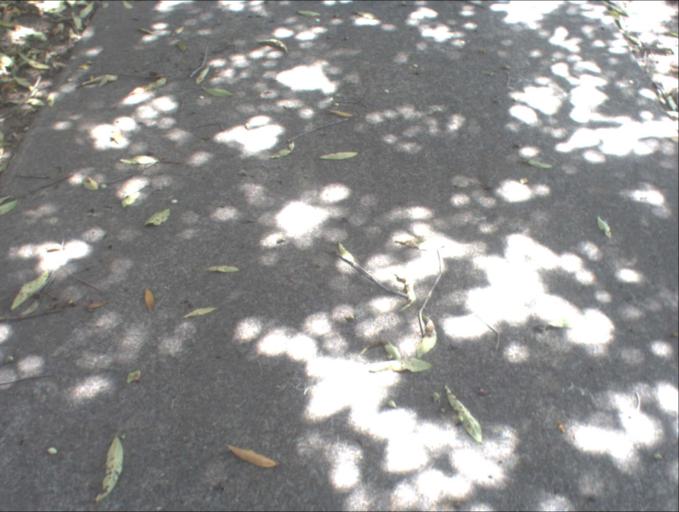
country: AU
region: Queensland
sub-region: Logan
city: Woodridge
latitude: -27.6193
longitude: 153.1021
